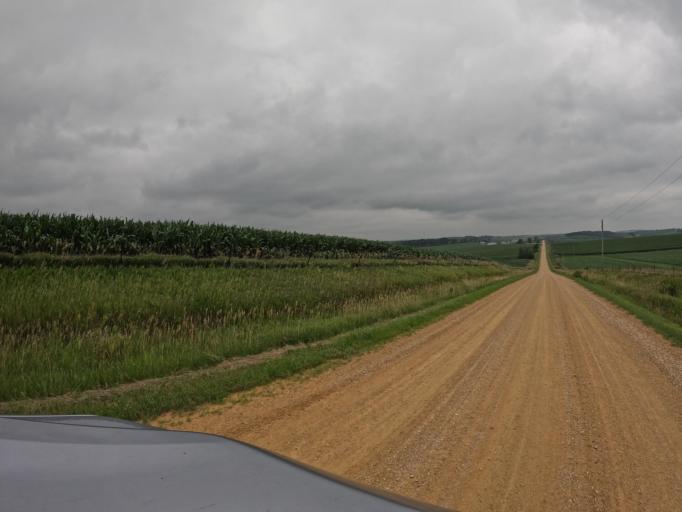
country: US
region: Illinois
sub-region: Carroll County
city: Savanna
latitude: 41.9825
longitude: -90.1804
